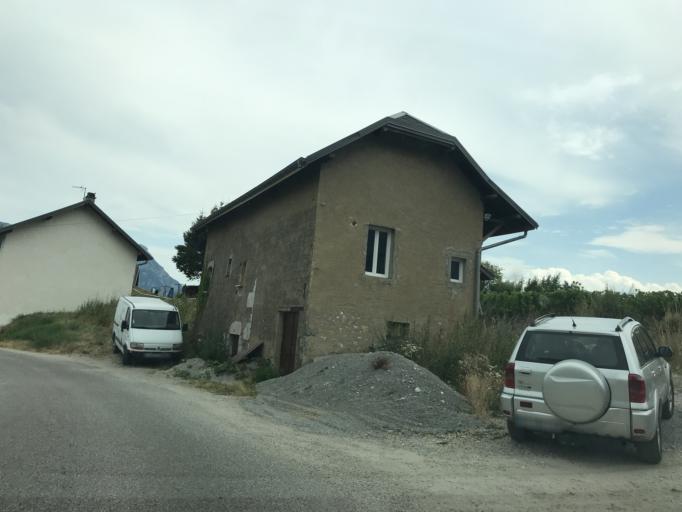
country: FR
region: Rhone-Alpes
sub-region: Departement de la Savoie
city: Les Marches
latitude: 45.4926
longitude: 5.9686
